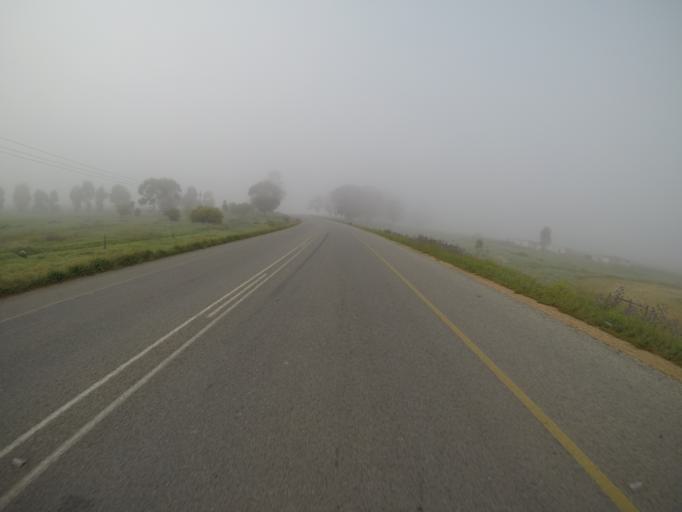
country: ZA
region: Western Cape
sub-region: City of Cape Town
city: Kraaifontein
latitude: -33.6927
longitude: 18.7039
